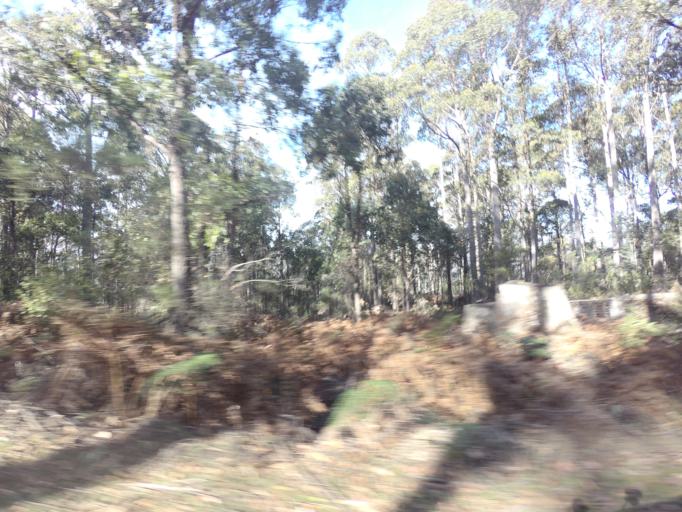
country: AU
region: Tasmania
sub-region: Sorell
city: Sorell
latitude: -42.4907
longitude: 147.4815
